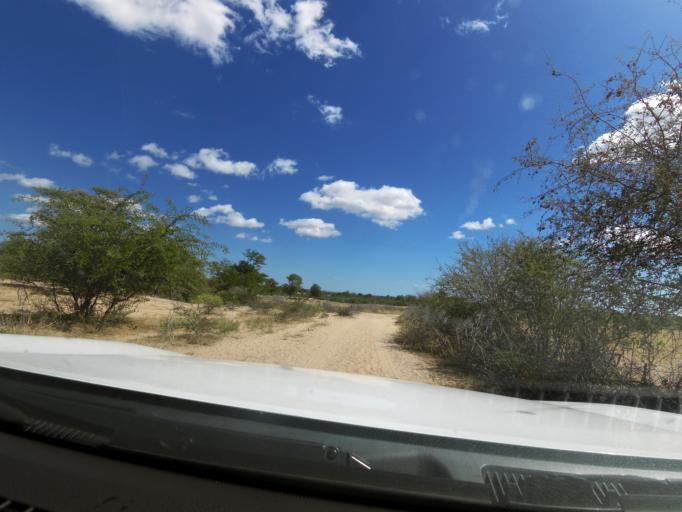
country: ZW
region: Matabeleland North
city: Kamativi Mine
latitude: -17.9987
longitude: 27.1356
